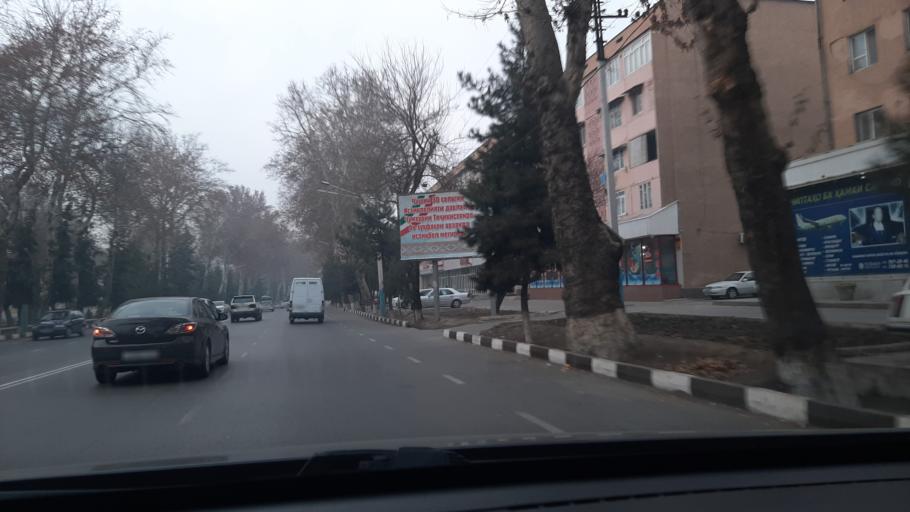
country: TJ
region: Viloyati Sughd
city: Khujand
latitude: 40.2686
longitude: 69.6478
